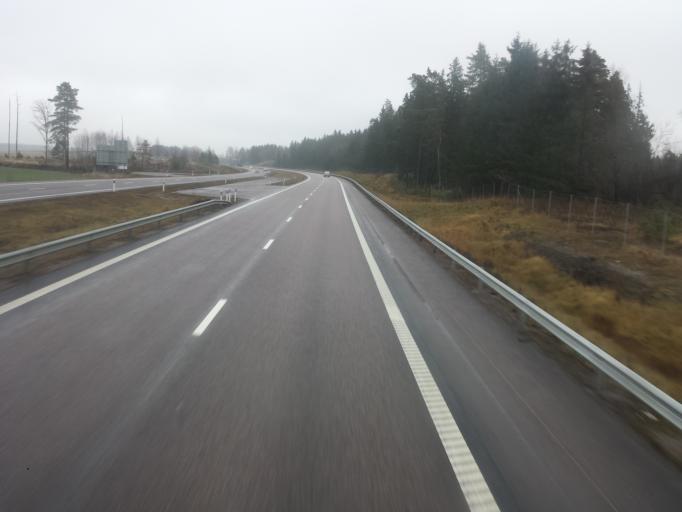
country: SE
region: Soedermanland
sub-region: Nykopings Kommun
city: Stigtomta
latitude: 58.7534
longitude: 16.7411
